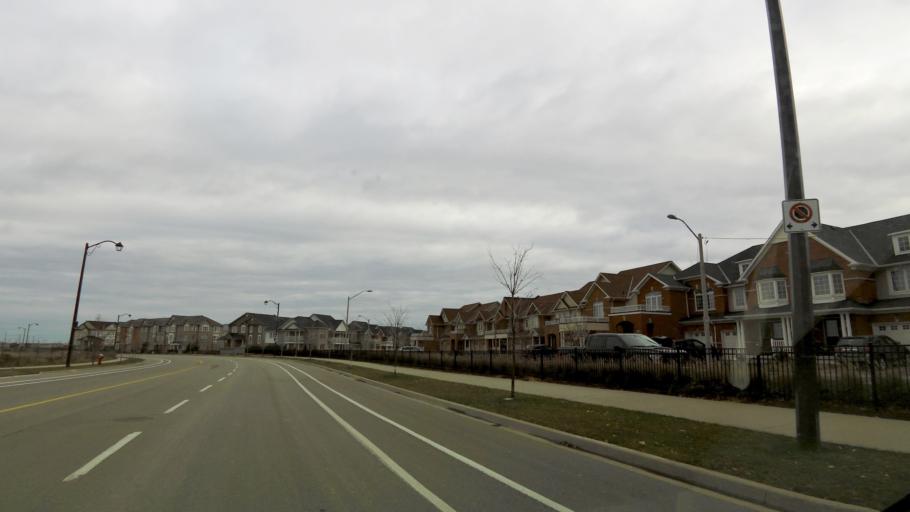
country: CA
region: Ontario
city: Burlington
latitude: 43.4110
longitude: -79.8202
